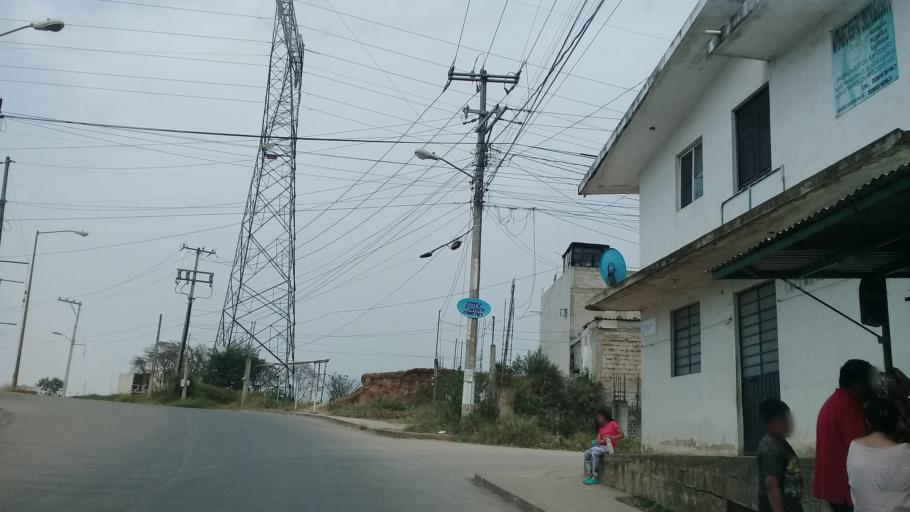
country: MX
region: Veracruz
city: El Castillo
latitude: 19.5593
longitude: -96.8874
